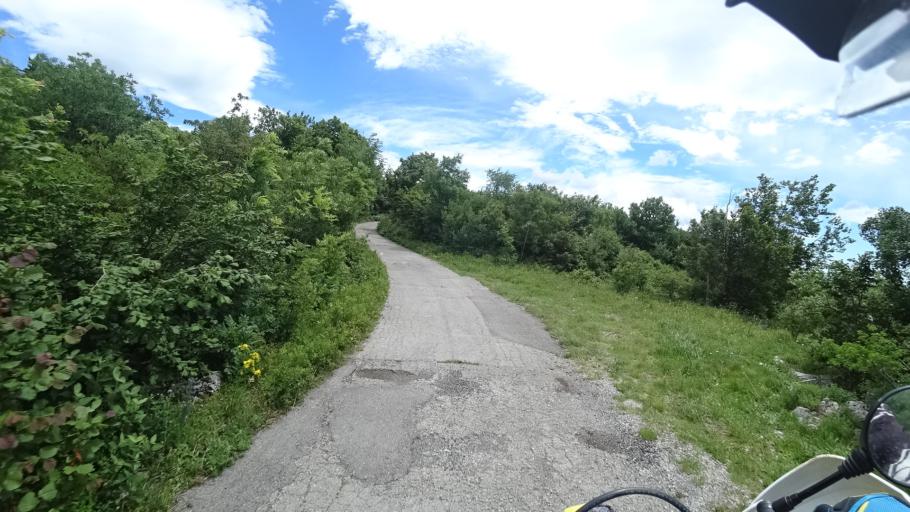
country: HR
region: Primorsko-Goranska
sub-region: Grad Crikvenica
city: Jadranovo
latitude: 45.2437
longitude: 14.6727
